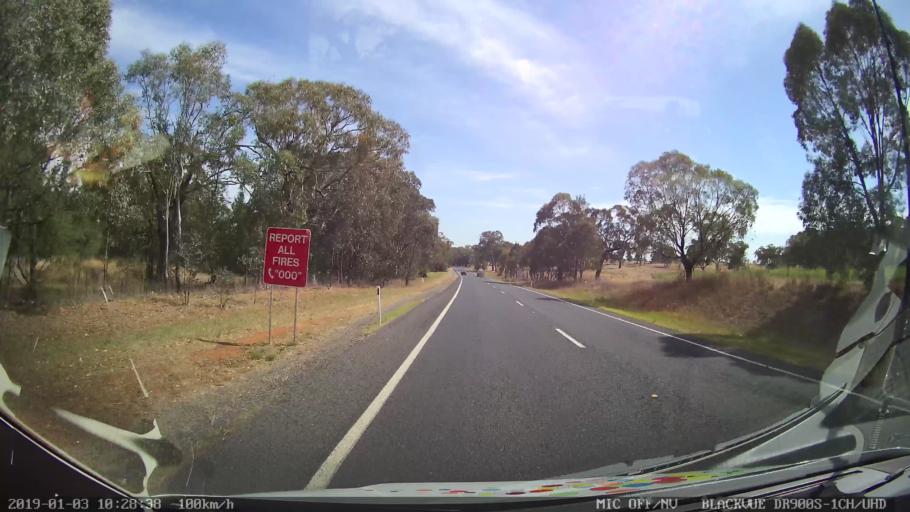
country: AU
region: New South Wales
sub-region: Young
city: Young
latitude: -34.3851
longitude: 148.2593
